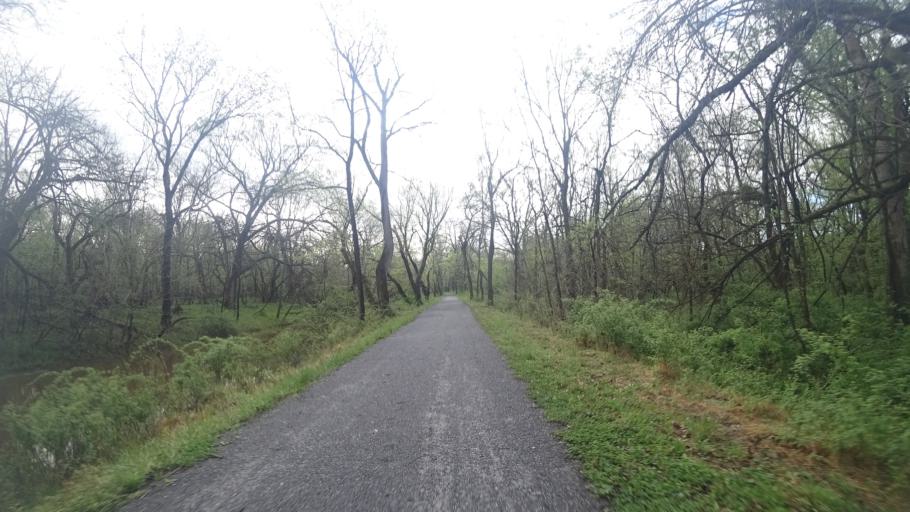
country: US
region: Virginia
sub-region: Loudoun County
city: Belmont
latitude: 39.1197
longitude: -77.5000
